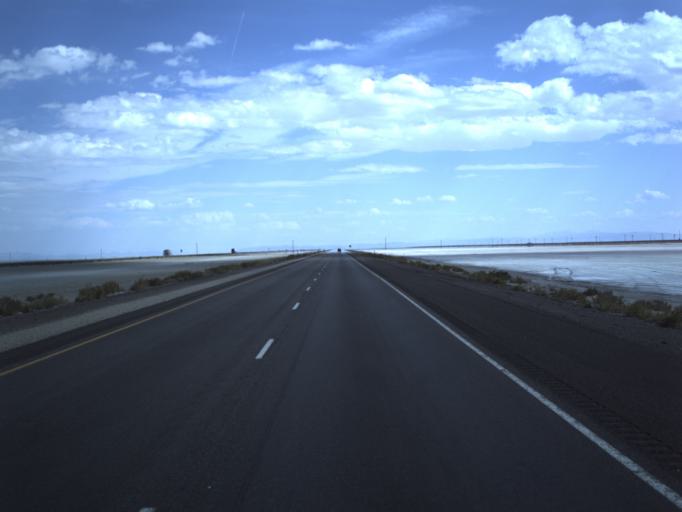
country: US
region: Utah
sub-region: Tooele County
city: Wendover
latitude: 40.7370
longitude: -113.7776
